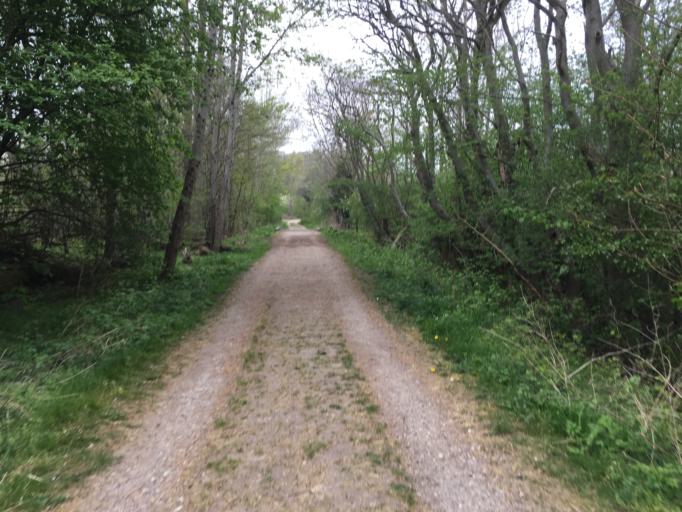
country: DK
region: South Denmark
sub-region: Odense Kommune
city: Hojby
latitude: 55.3527
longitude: 10.4377
